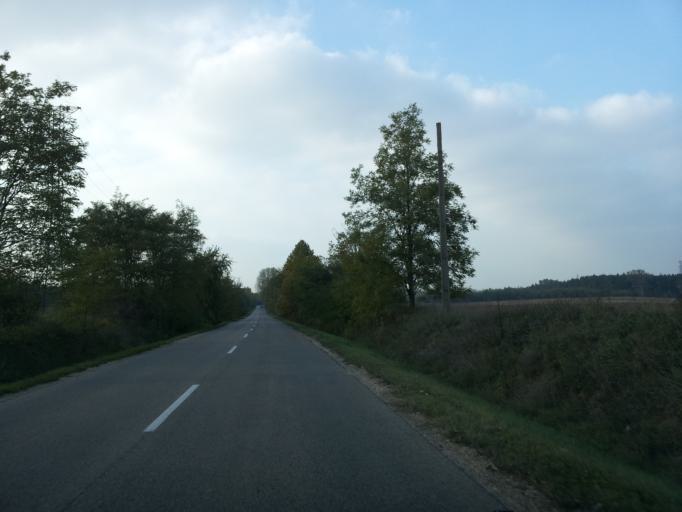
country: HU
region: Komarom-Esztergom
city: Oroszlany
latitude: 47.4780
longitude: 18.2840
